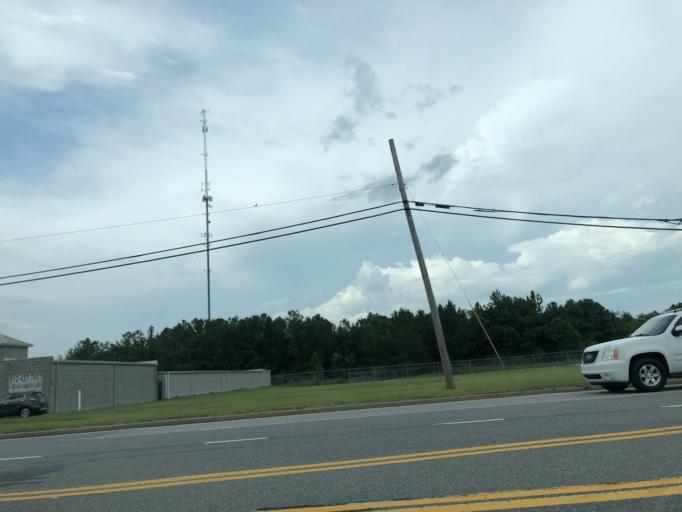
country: US
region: Georgia
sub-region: Wayne County
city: Jesup
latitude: 31.6202
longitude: -81.9010
